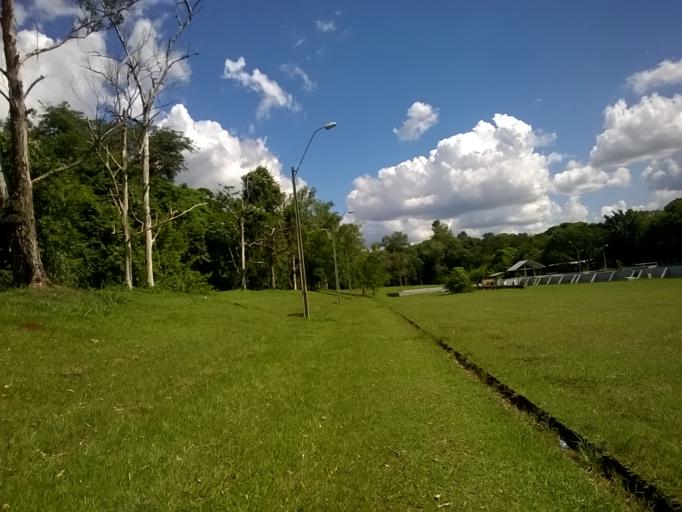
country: PY
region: Alto Parana
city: Ciudad del Este
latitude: -25.4425
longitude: -54.6350
